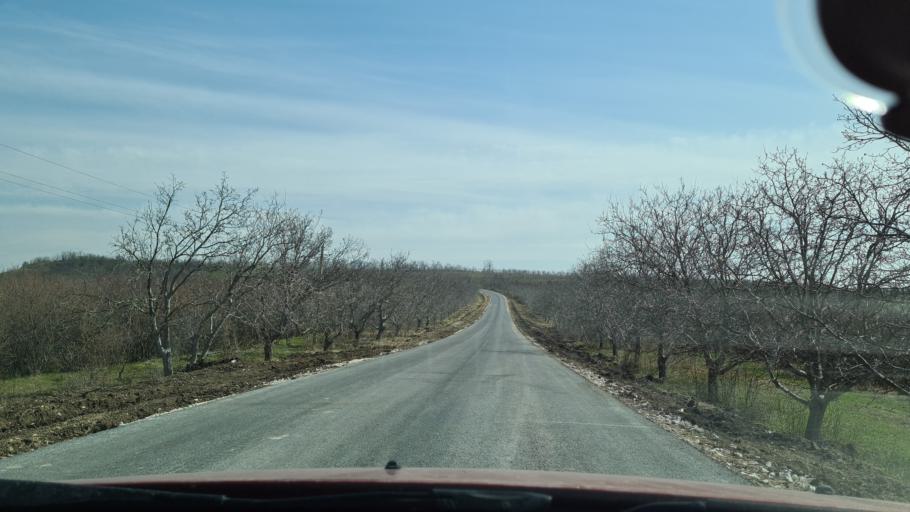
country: MD
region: Ungheni
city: Ungheni
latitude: 47.2629
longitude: 27.9703
